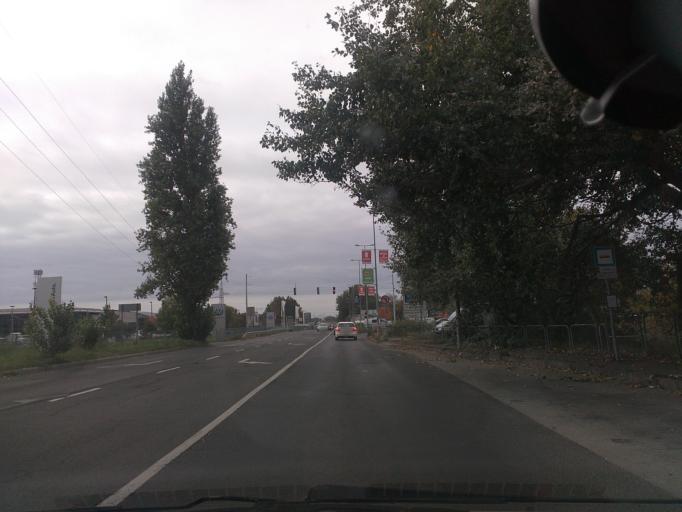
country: HU
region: Budapest
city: Budapest XVIII. keruelet
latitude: 47.4247
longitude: 19.1579
